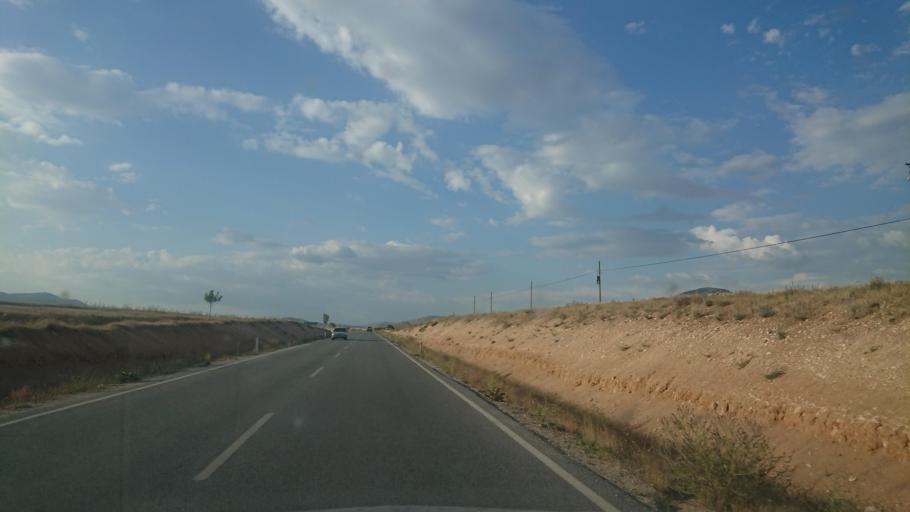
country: TR
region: Aksaray
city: Aksaray
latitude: 38.5151
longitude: 34.0907
